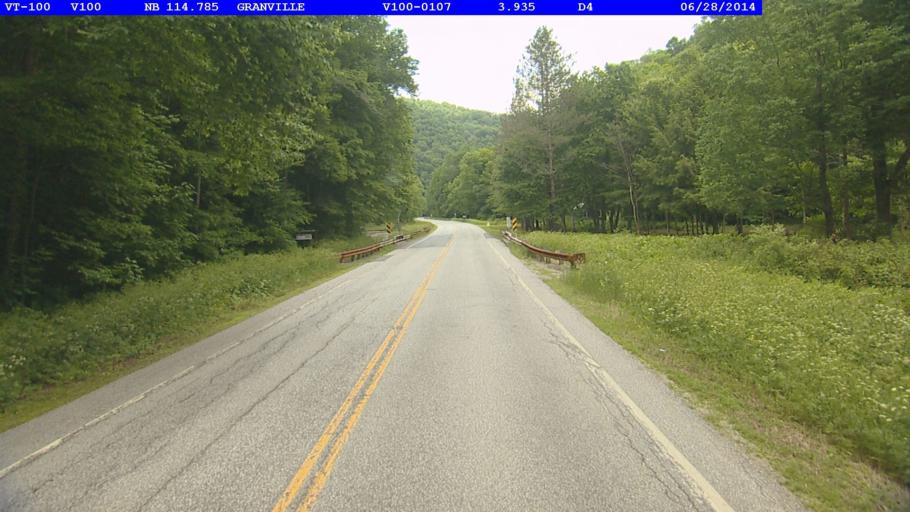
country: US
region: Vermont
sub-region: Orange County
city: Randolph
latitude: 43.9981
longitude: -72.8523
